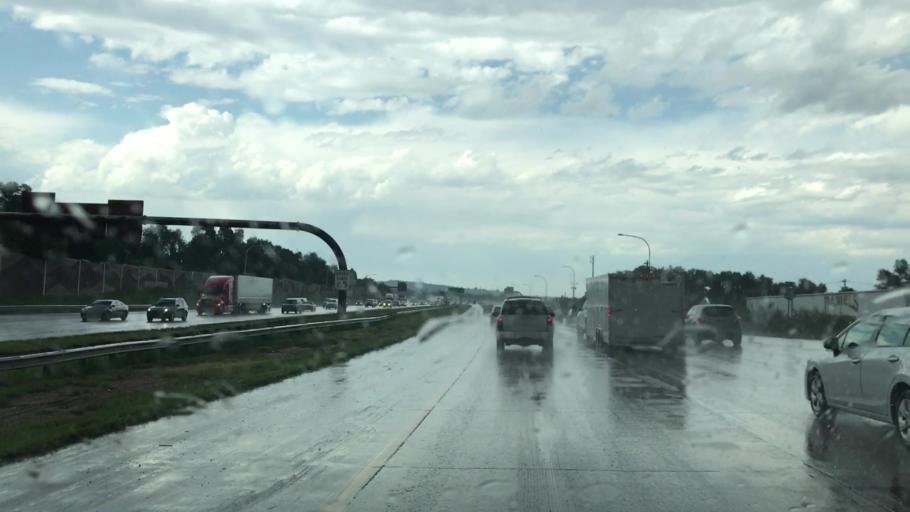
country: US
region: Colorado
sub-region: El Paso County
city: Colorado Springs
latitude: 38.8648
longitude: -104.8333
